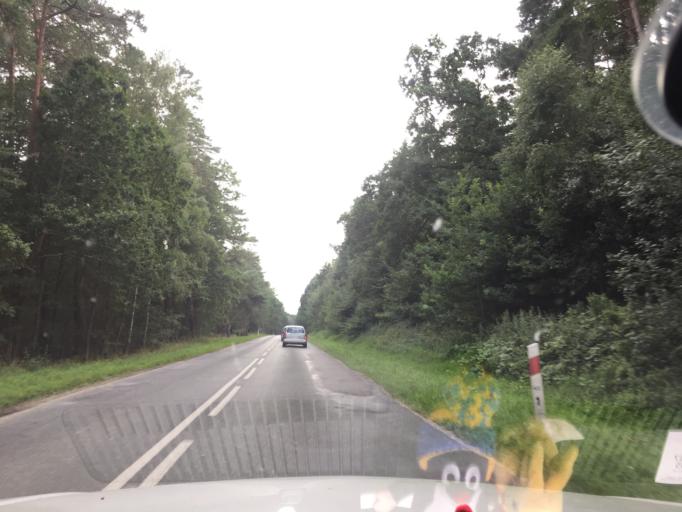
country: PL
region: West Pomeranian Voivodeship
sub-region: Powiat gryficki
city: Pobierowo
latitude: 54.0624
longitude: 14.9595
